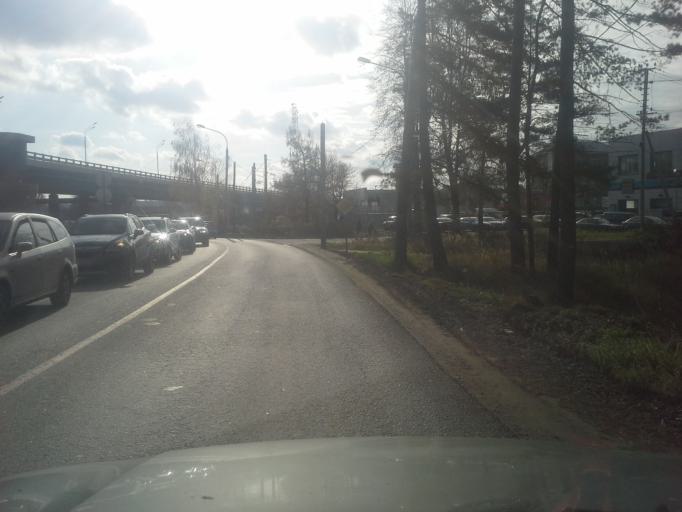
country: RU
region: Moskovskaya
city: Zvenigorod
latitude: 55.7016
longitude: 36.8812
